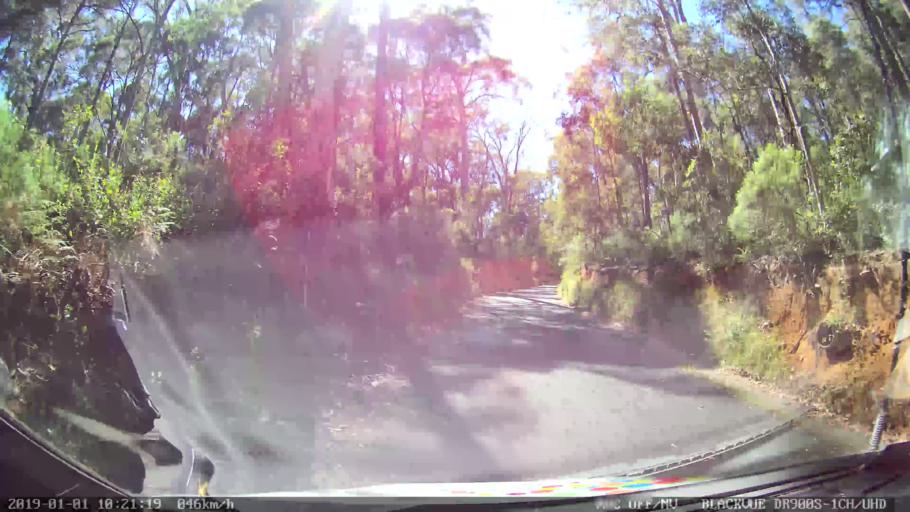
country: AU
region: New South Wales
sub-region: Snowy River
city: Jindabyne
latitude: -36.0755
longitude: 148.1946
